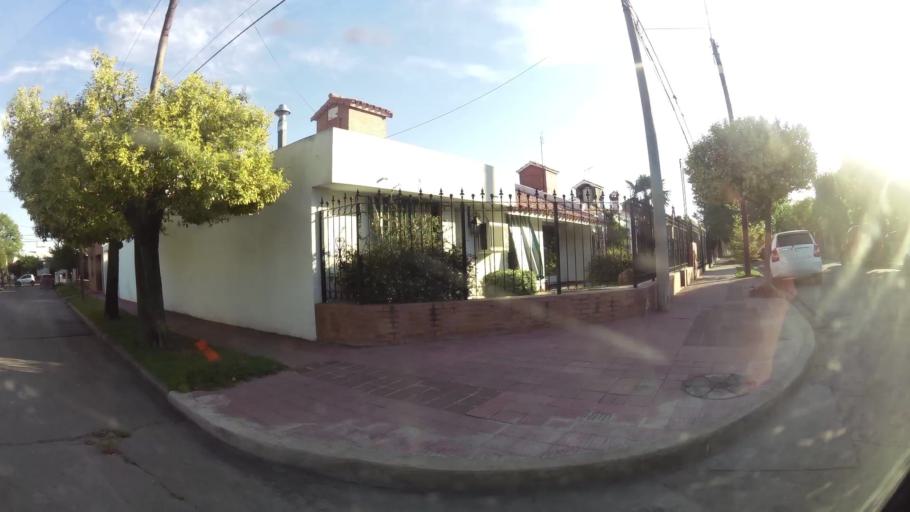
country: AR
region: Cordoba
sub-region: Departamento de Capital
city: Cordoba
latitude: -31.3885
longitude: -64.2179
